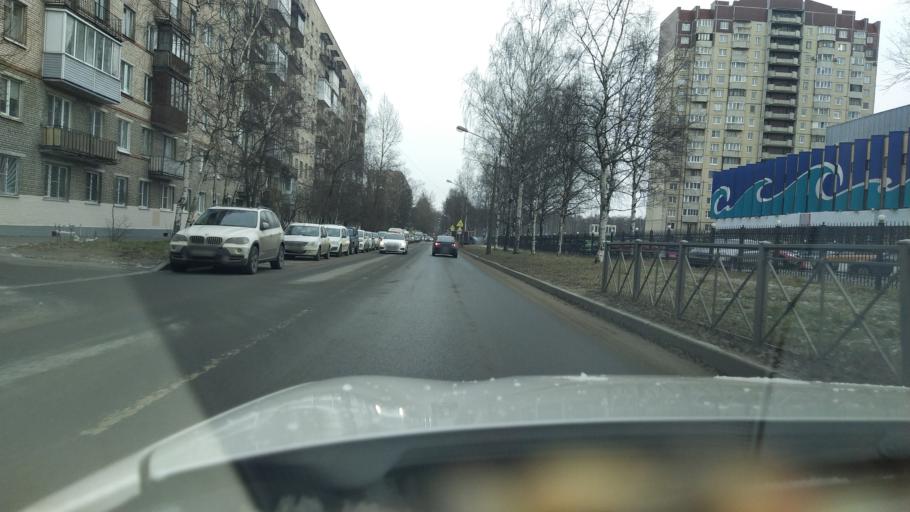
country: RU
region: Leningrad
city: Kalininskiy
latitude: 60.0014
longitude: 30.3877
